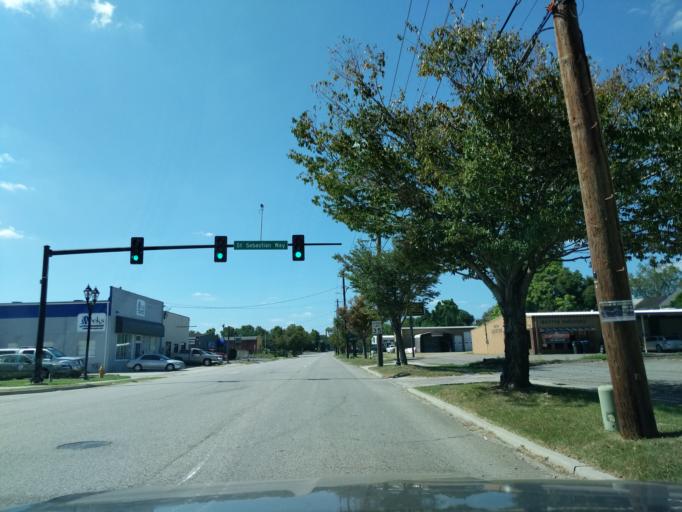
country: US
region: Georgia
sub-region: Richmond County
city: Augusta
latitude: 33.4814
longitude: -81.9788
